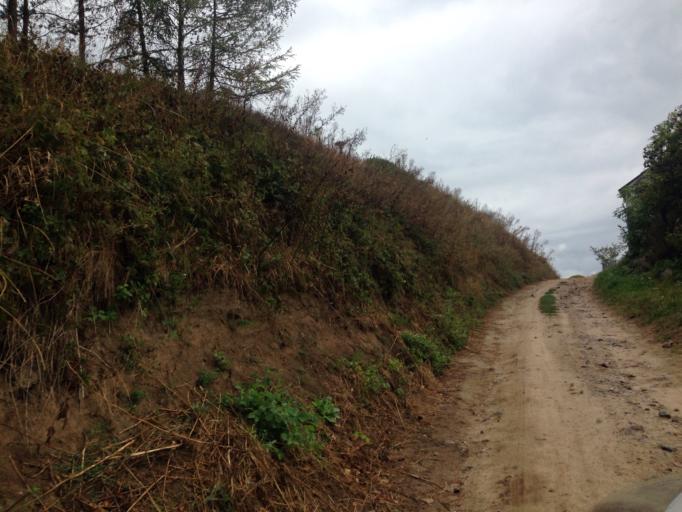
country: PL
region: Kujawsko-Pomorskie
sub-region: Powiat brodnicki
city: Bartniczka
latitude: 53.2703
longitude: 19.6437
